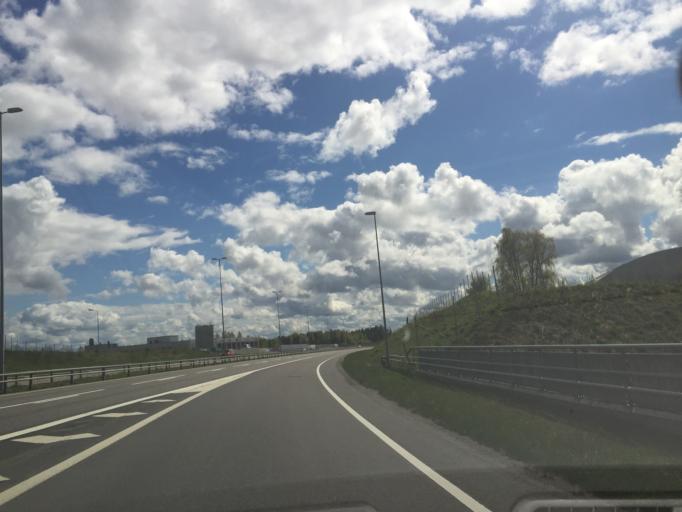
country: NO
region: Akershus
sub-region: Eidsvoll
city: Raholt
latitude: 60.2525
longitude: 11.1815
